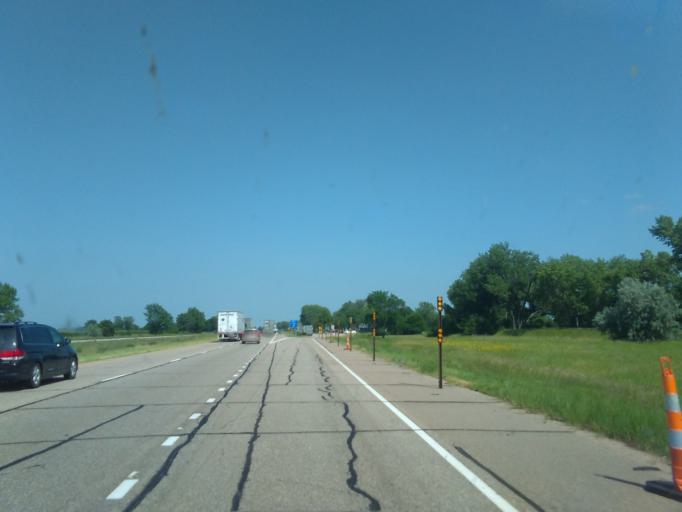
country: US
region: Nebraska
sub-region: Buffalo County
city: Kearney
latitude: 40.6712
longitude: -99.1614
